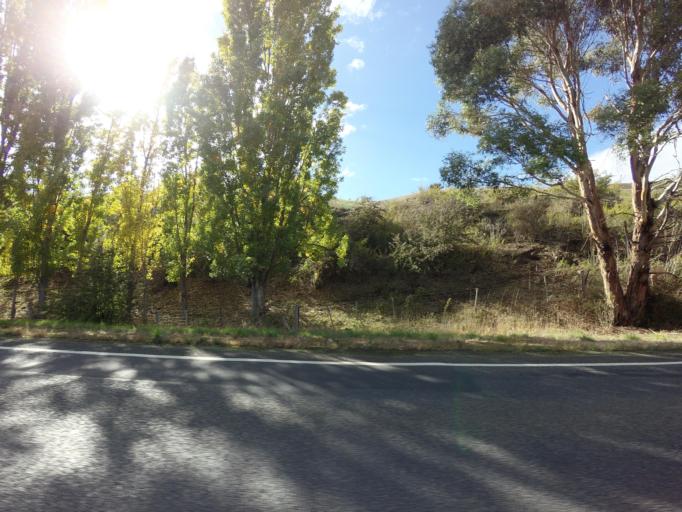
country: AU
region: Tasmania
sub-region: Derwent Valley
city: New Norfolk
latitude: -42.7312
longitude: 146.9567
